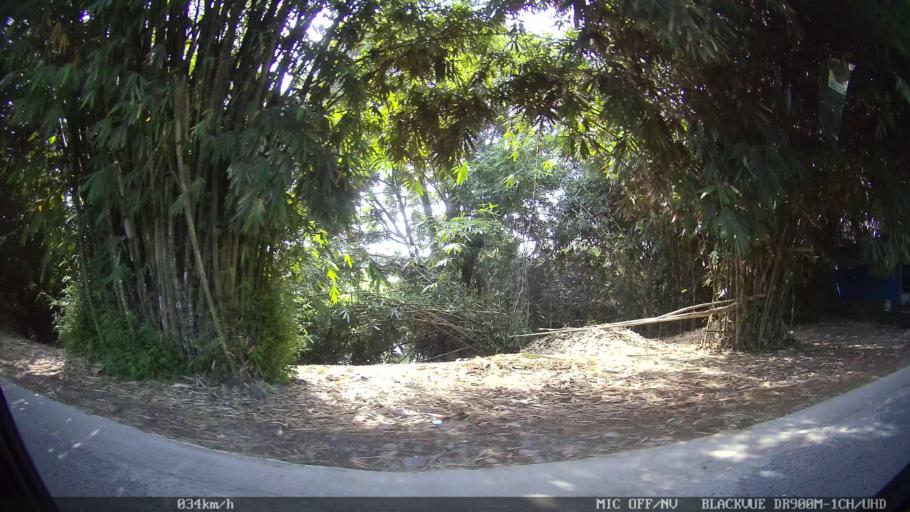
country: ID
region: Lampung
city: Kedaton
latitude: -5.3415
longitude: 105.2722
